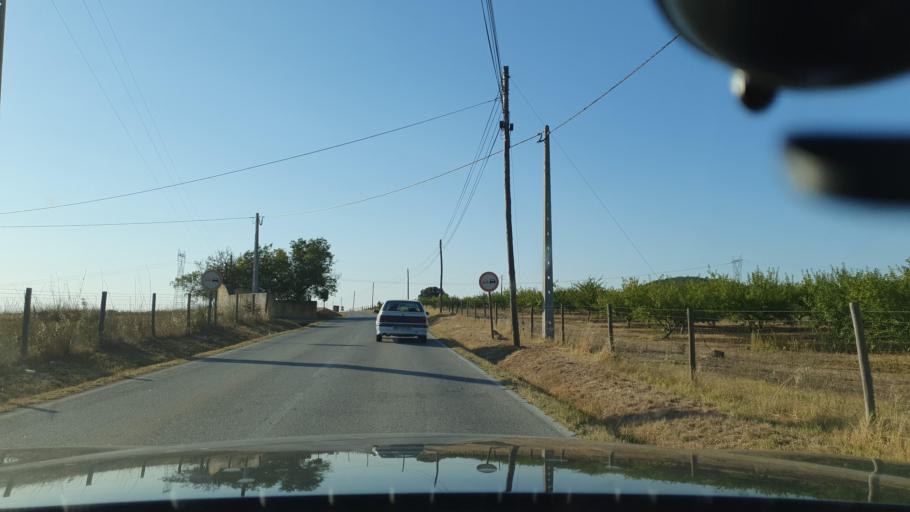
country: PT
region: Evora
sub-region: Estremoz
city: Estremoz
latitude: 38.8645
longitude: -7.6217
